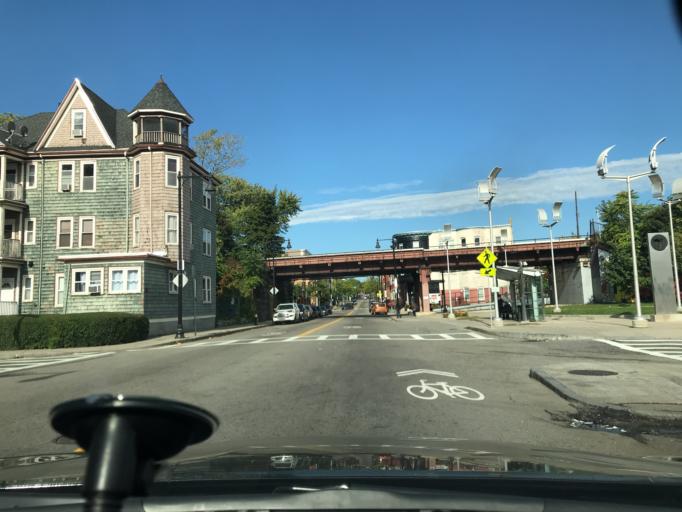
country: US
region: Massachusetts
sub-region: Suffolk County
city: South Boston
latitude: 42.2987
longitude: -71.0635
